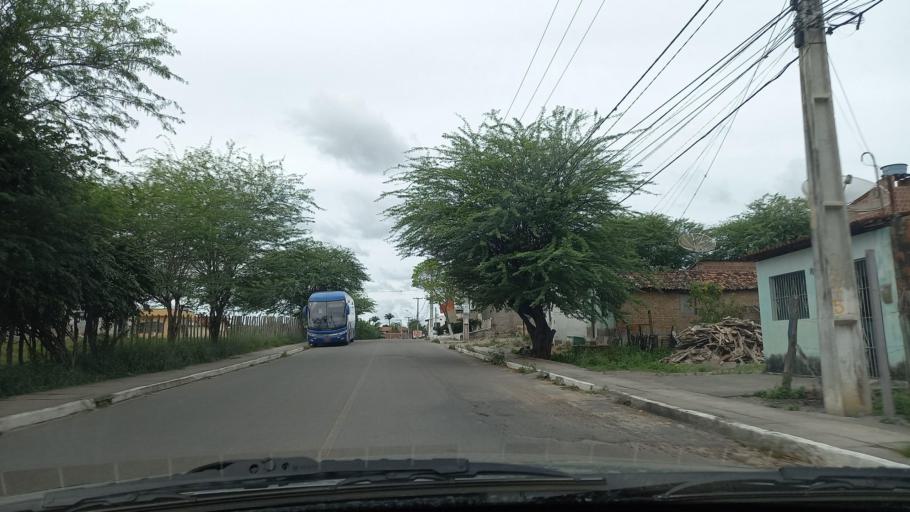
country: BR
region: Pernambuco
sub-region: Gravata
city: Gravata
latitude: -8.2063
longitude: -35.5838
